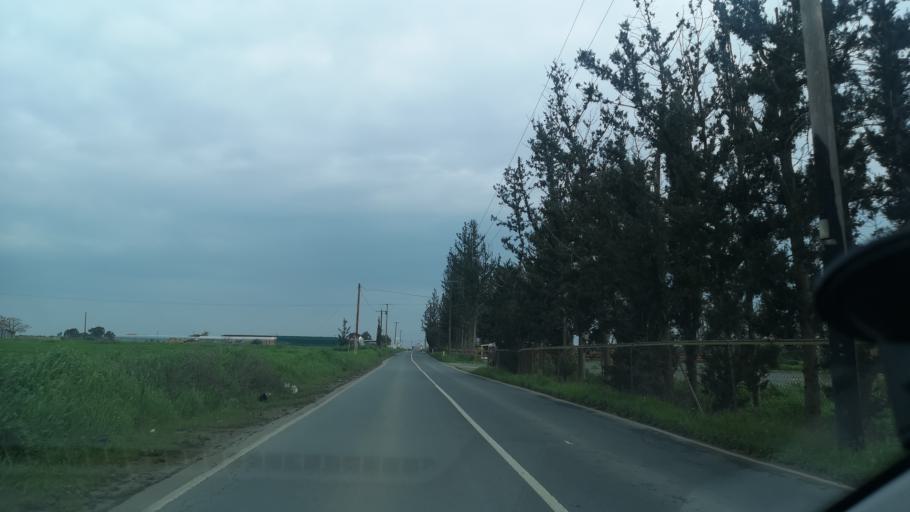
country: CY
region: Lefkosia
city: Tseri
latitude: 35.0820
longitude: 33.3003
